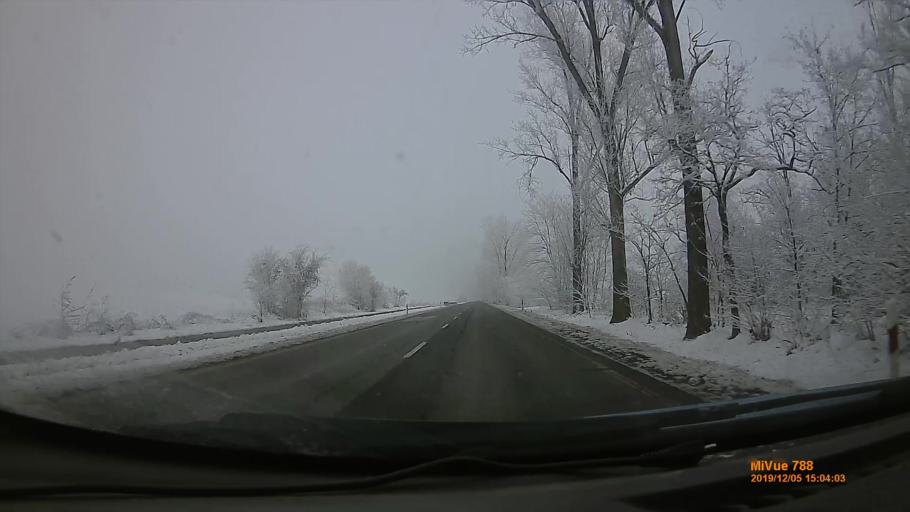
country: HU
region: Szabolcs-Szatmar-Bereg
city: Tiszanagyfalu
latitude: 48.0916
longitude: 21.4954
